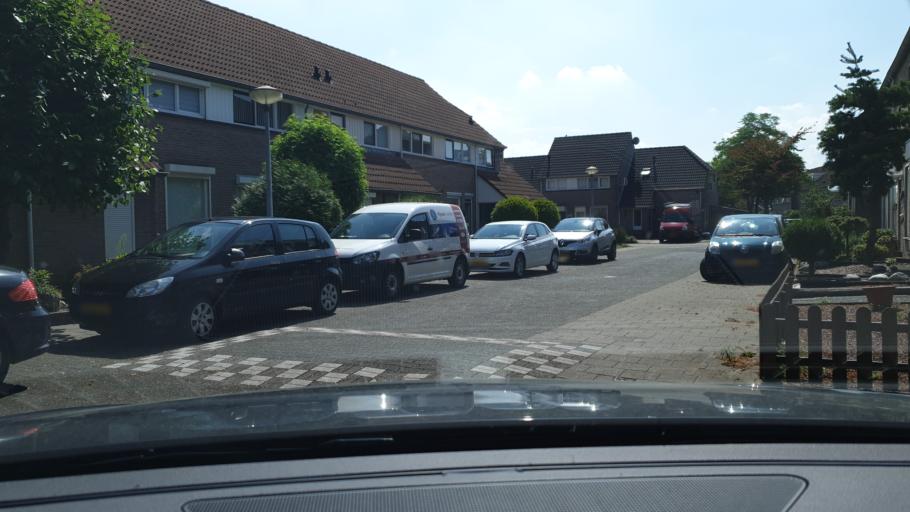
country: NL
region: North Brabant
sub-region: Gemeente Eindhoven
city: Meerhoven
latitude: 51.4854
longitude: 5.4408
